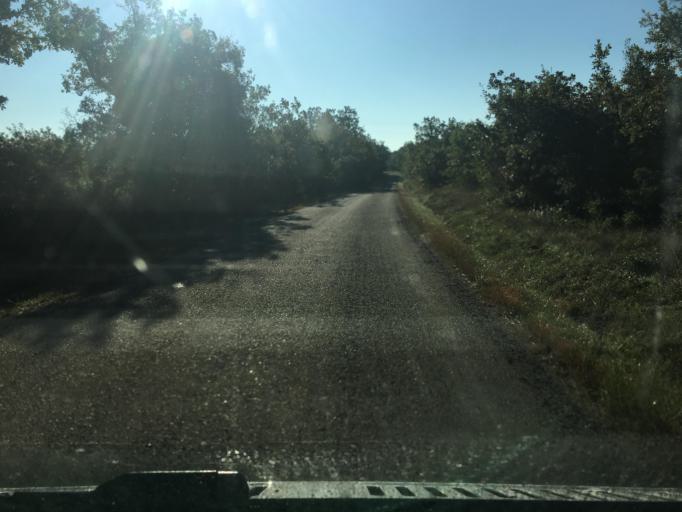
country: FR
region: Languedoc-Roussillon
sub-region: Departement du Gard
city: Goudargues
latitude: 44.1754
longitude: 4.3414
